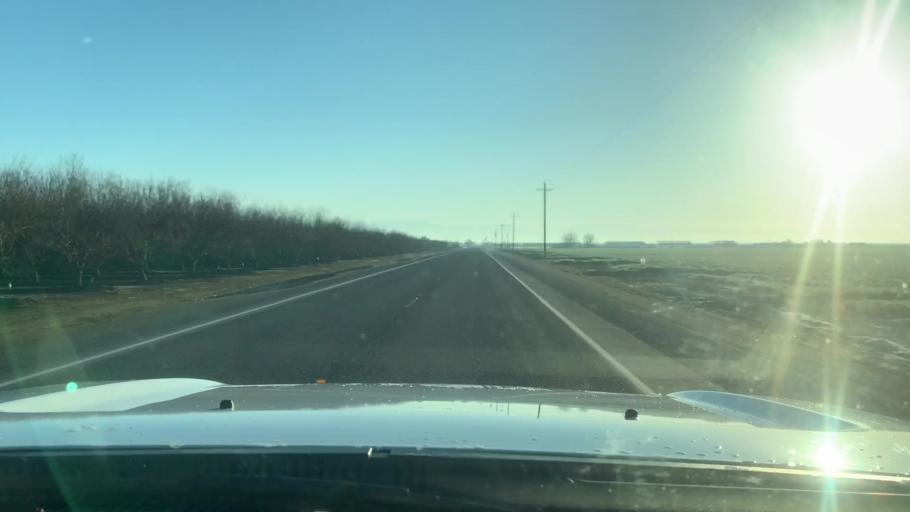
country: US
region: California
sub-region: Kings County
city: Home Garden
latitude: 36.2110
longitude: -119.5740
